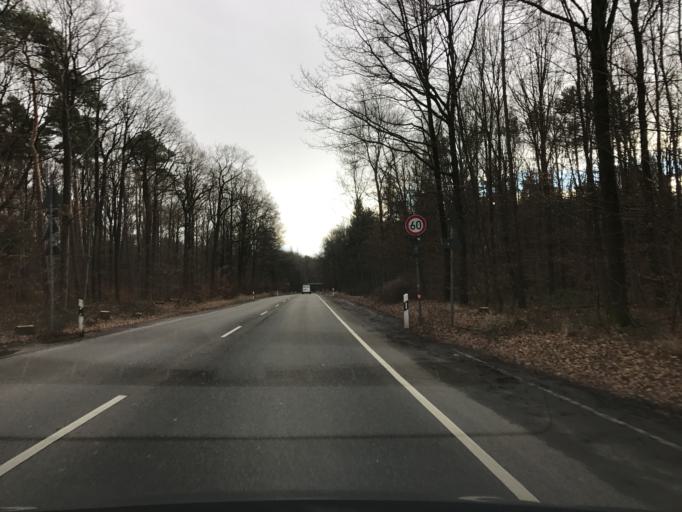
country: DE
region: Baden-Wuerttemberg
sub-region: Regierungsbezirk Stuttgart
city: Stuttgart-Ost
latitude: 48.7519
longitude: 9.1959
